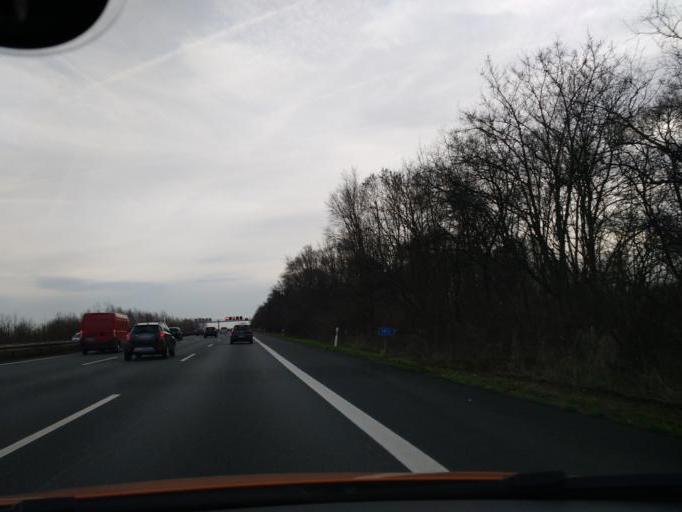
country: DE
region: Lower Saxony
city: Peine
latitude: 52.3501
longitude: 10.2008
